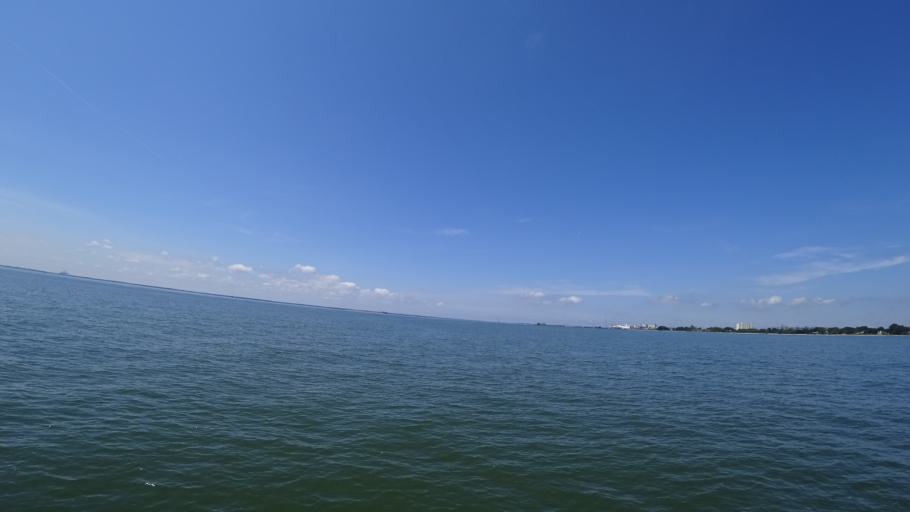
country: US
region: Virginia
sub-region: City of Newport News
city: Newport News
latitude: 36.9739
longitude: -76.3900
